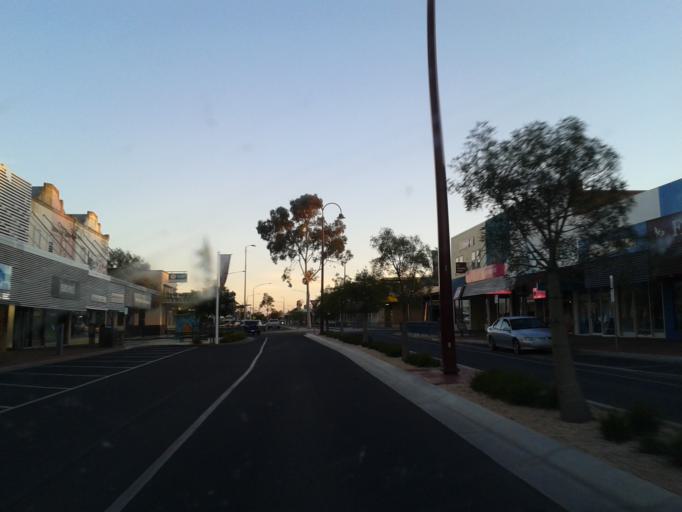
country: AU
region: Victoria
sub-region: Swan Hill
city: Swan Hill
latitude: -35.3401
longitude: 143.5599
